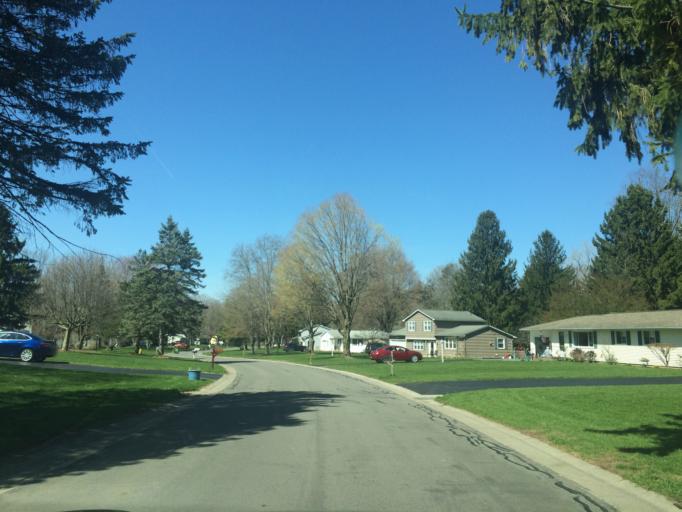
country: US
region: New York
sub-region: Monroe County
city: Fairport
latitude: 43.0942
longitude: -77.4627
